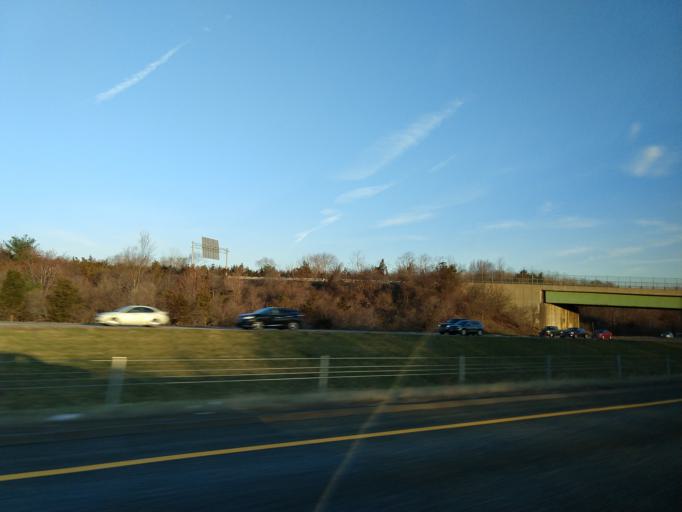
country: US
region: Massachusetts
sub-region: Essex County
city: Danvers
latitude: 42.5912
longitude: -70.9611
